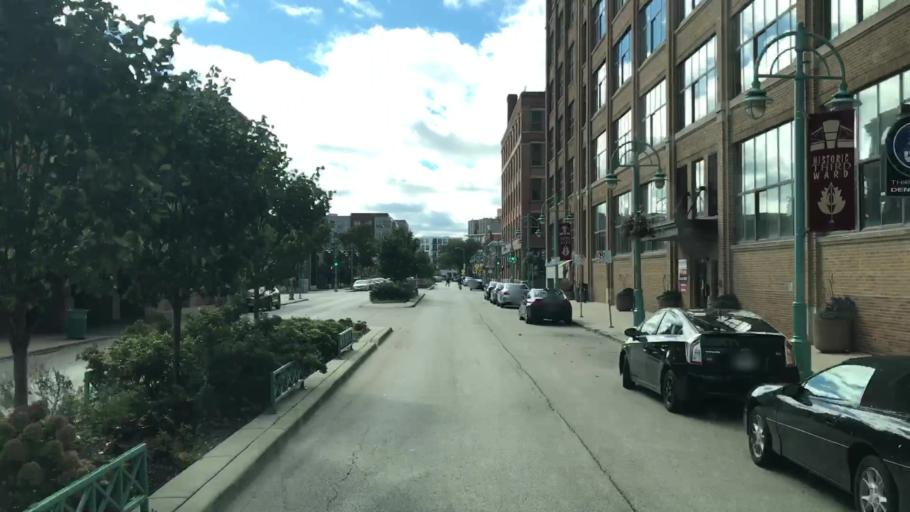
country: US
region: Wisconsin
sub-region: Milwaukee County
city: Milwaukee
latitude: 43.0335
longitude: -87.9060
